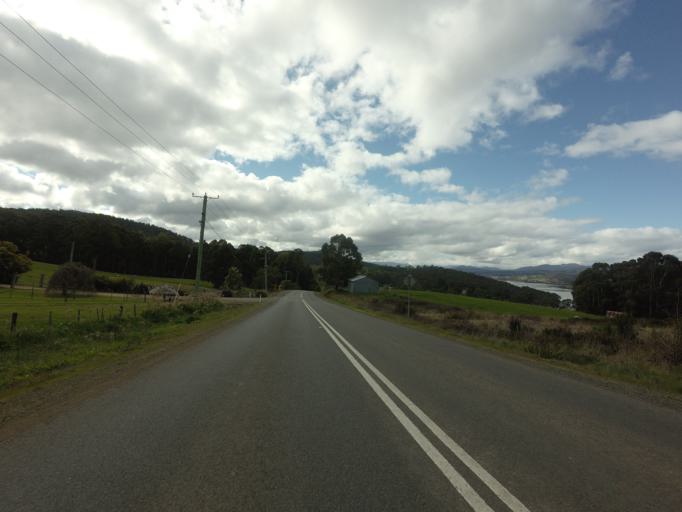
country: AU
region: Tasmania
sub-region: Huon Valley
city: Geeveston
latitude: -43.1960
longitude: 146.9569
